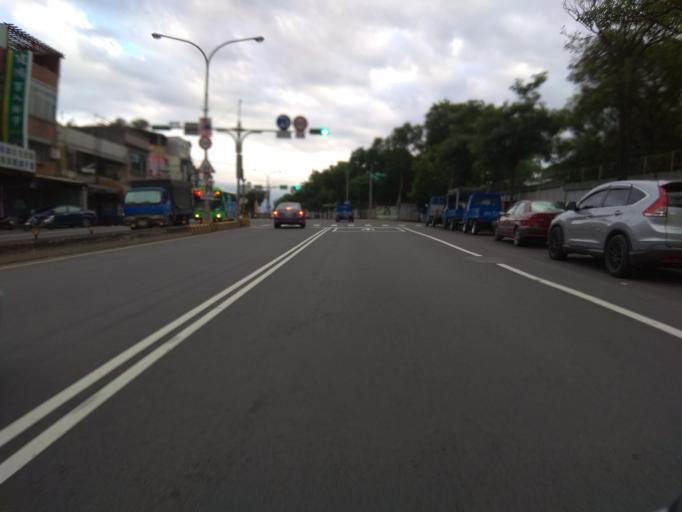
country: TW
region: Taiwan
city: Daxi
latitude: 24.8947
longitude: 121.2114
